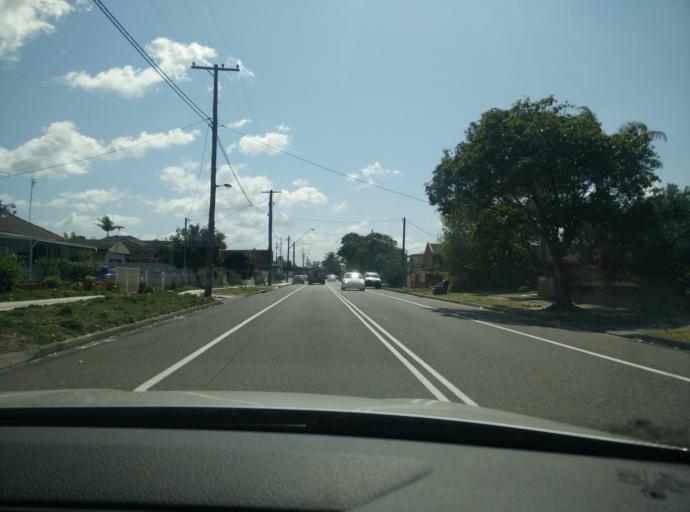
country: AU
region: New South Wales
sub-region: Gosford Shire
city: Umina
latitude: -33.5229
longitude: 151.3164
